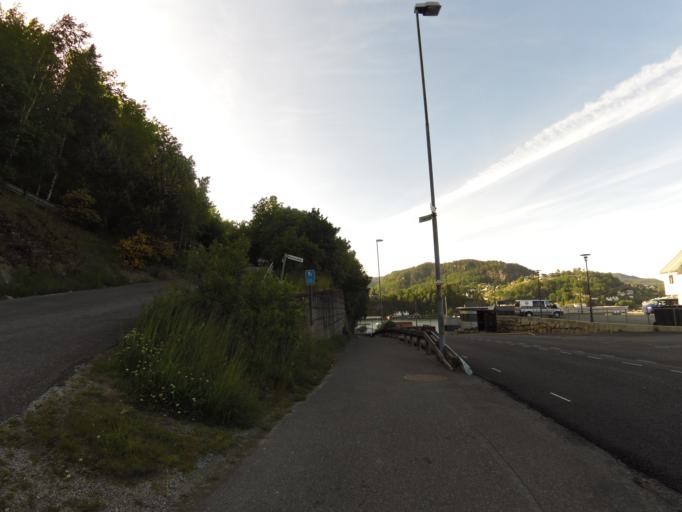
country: NO
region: Vest-Agder
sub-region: Flekkefjord
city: Flekkefjord
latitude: 58.2907
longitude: 6.6485
